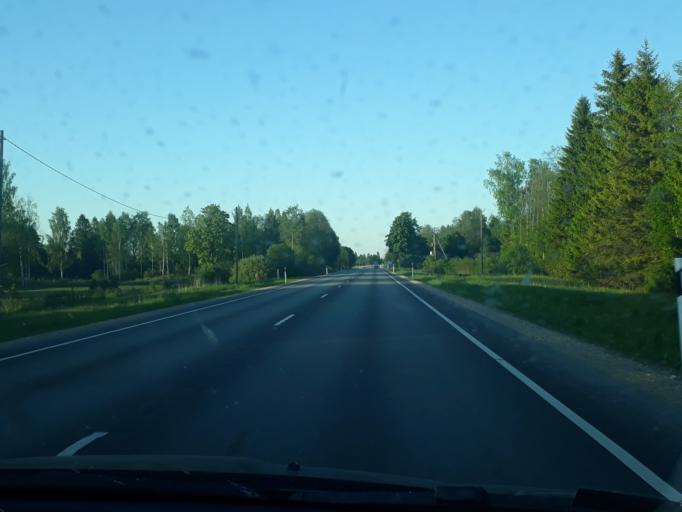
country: EE
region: Paernumaa
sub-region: Tootsi vald
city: Tootsi
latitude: 58.4892
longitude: 24.7541
